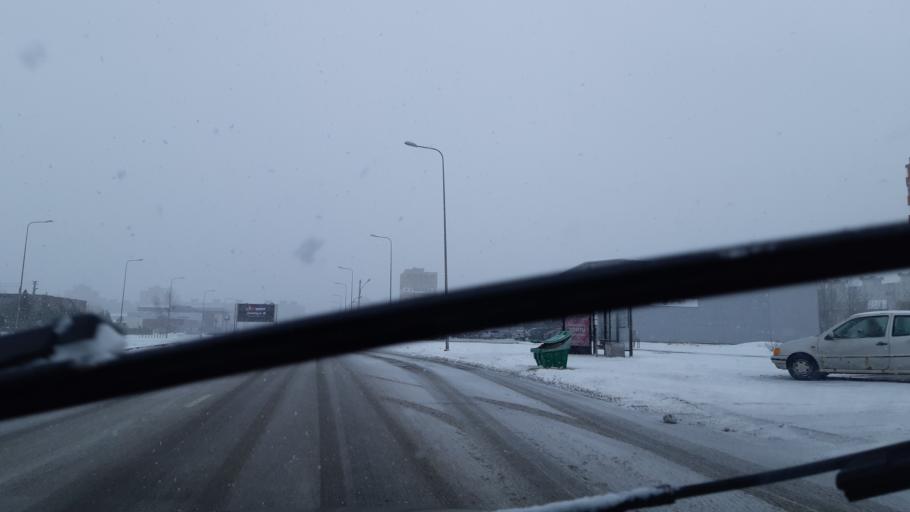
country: LT
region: Kauno apskritis
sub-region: Kaunas
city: Silainiai
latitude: 54.9276
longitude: 23.8794
